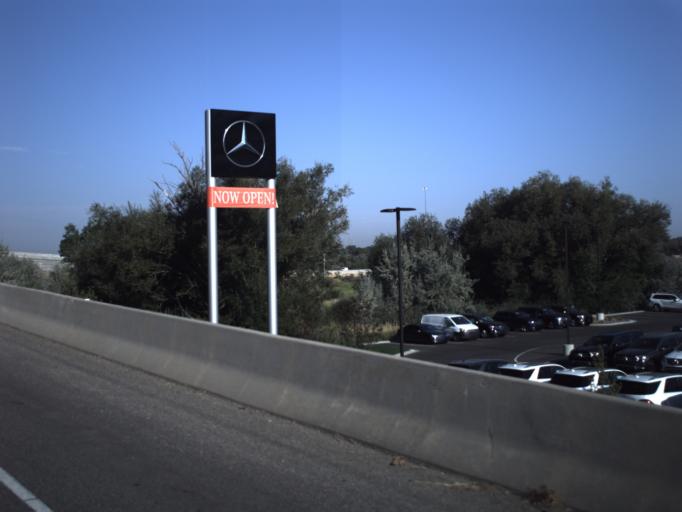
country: US
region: Utah
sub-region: Davis County
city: Farmington
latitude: 40.9914
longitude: -111.9000
